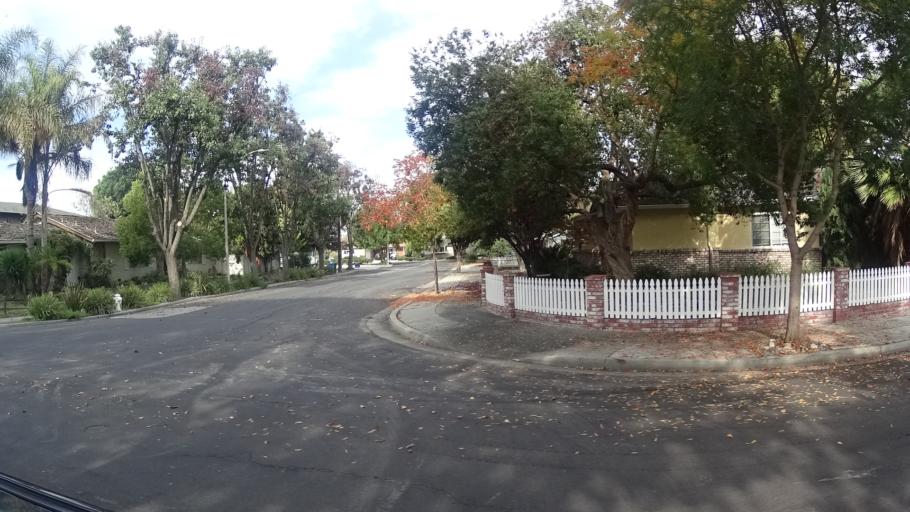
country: US
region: California
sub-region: Santa Clara County
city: Santa Clara
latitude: 37.3421
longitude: -121.9391
